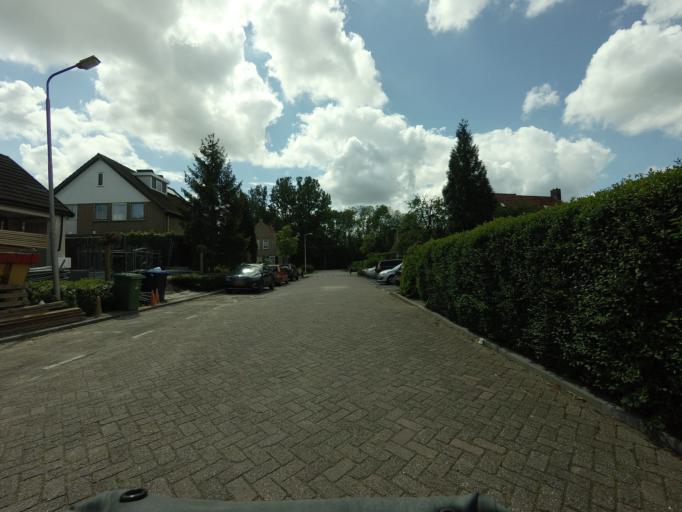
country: NL
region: South Holland
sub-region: Gemeente Giessenlanden
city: Giessenburg
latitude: 51.8430
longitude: 4.9270
